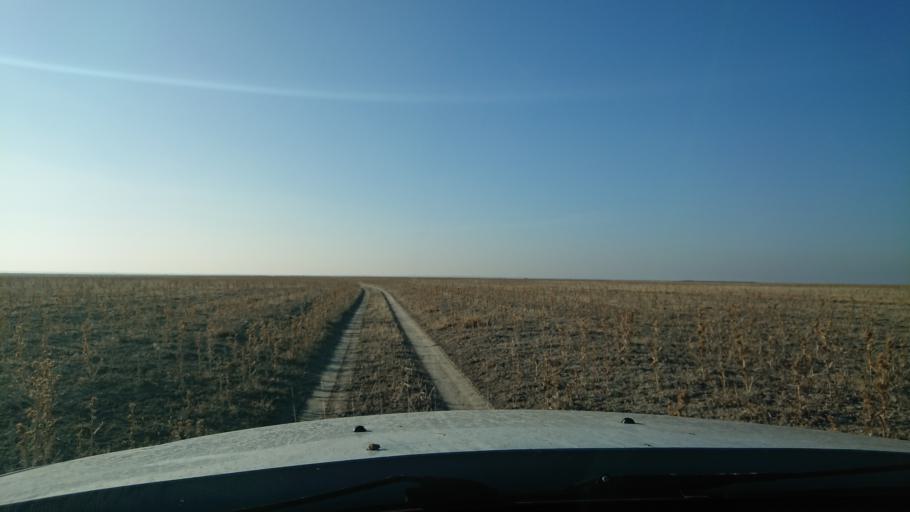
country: TR
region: Aksaray
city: Sultanhani
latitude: 38.3718
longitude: 33.5450
